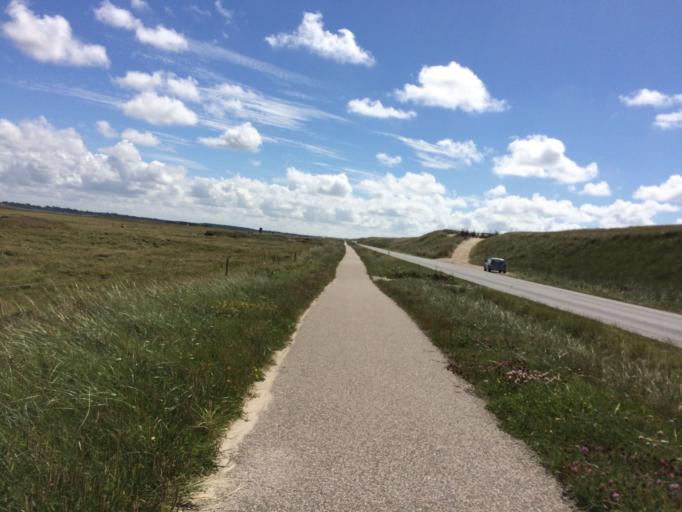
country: DK
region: Central Jutland
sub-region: Holstebro Kommune
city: Ulfborg
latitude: 56.3511
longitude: 8.1226
